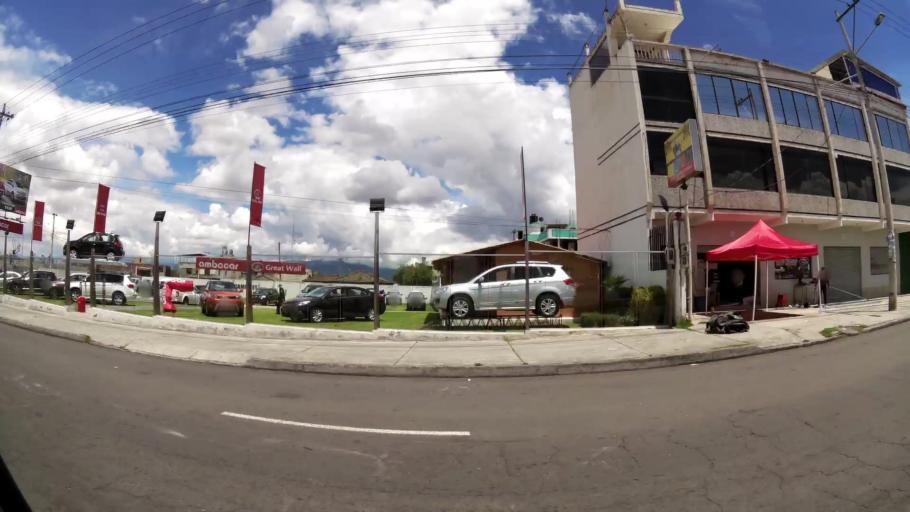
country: EC
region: Tungurahua
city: Ambato
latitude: -1.2751
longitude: -78.6108
